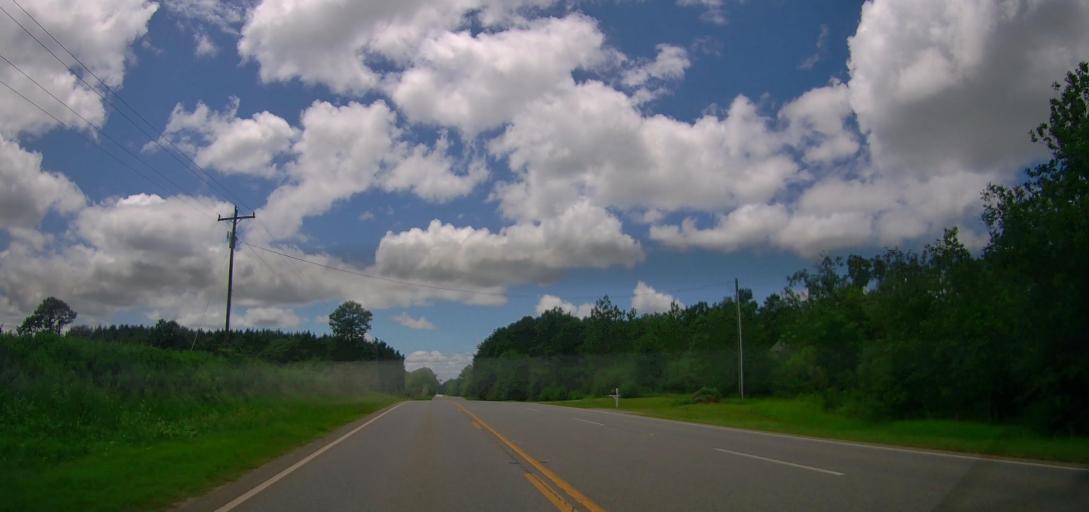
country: US
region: Georgia
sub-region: Turner County
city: Ashburn
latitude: 31.7221
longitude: -83.5485
